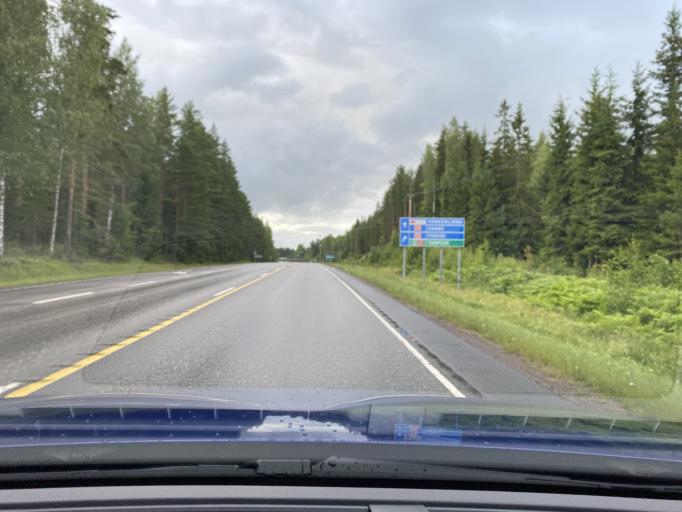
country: FI
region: Uusimaa
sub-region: Helsinki
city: Hyvinge
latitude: 60.5592
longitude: 24.8195
